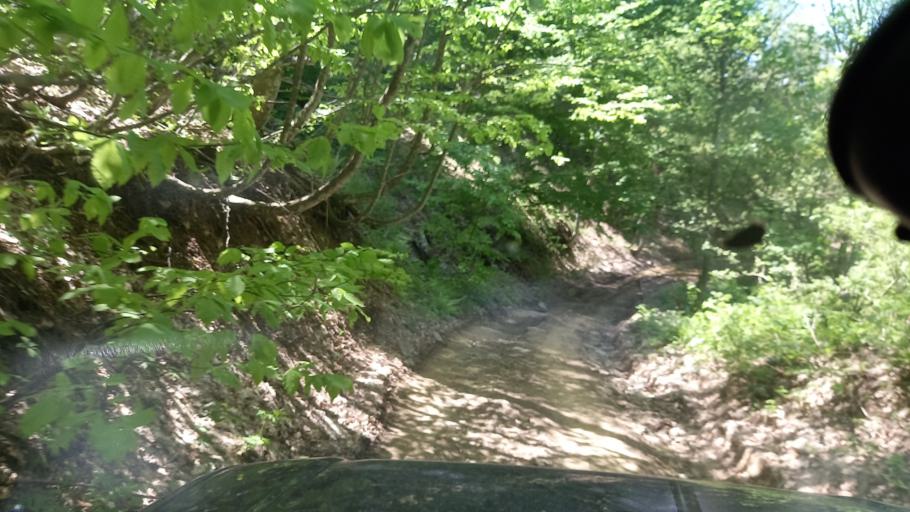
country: RU
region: Krasnodarskiy
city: Tuapse
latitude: 44.2502
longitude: 39.2951
